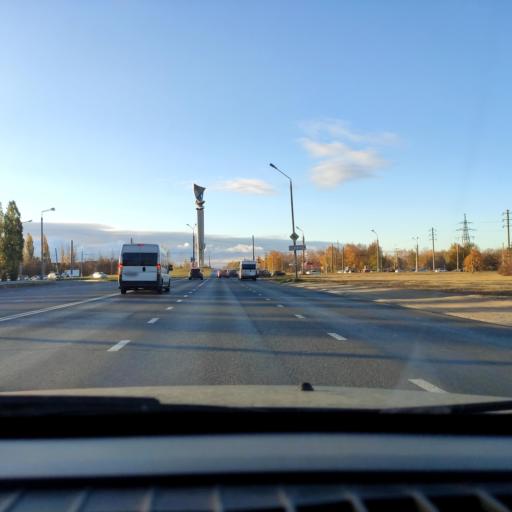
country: RU
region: Samara
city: Tol'yatti
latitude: 53.5550
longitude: 49.2880
